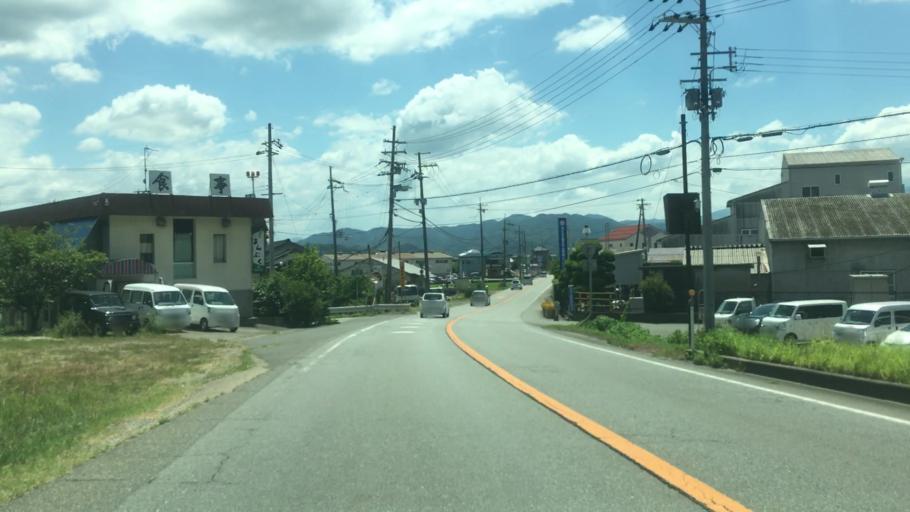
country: JP
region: Hyogo
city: Toyooka
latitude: 35.4996
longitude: 134.8058
